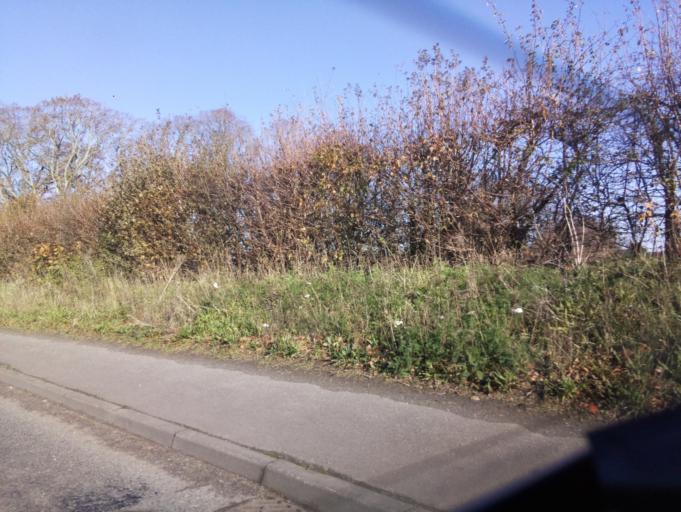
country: GB
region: England
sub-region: Somerset
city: Yeovil
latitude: 50.9295
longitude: -2.6398
